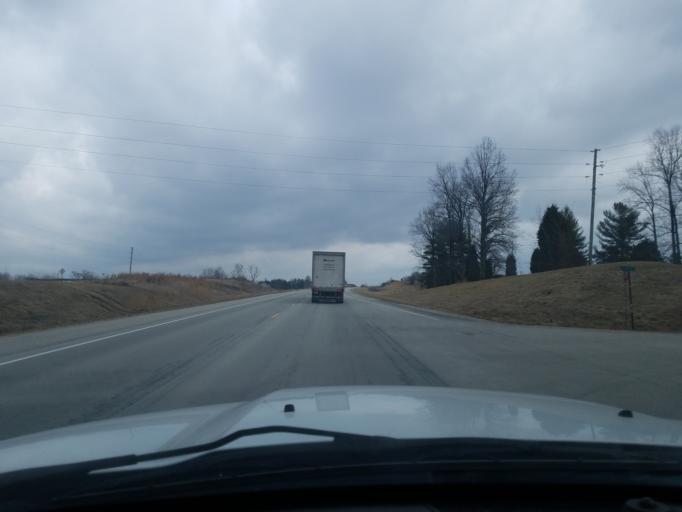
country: US
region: Indiana
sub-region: Crawford County
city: English
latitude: 38.2025
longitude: -86.5971
